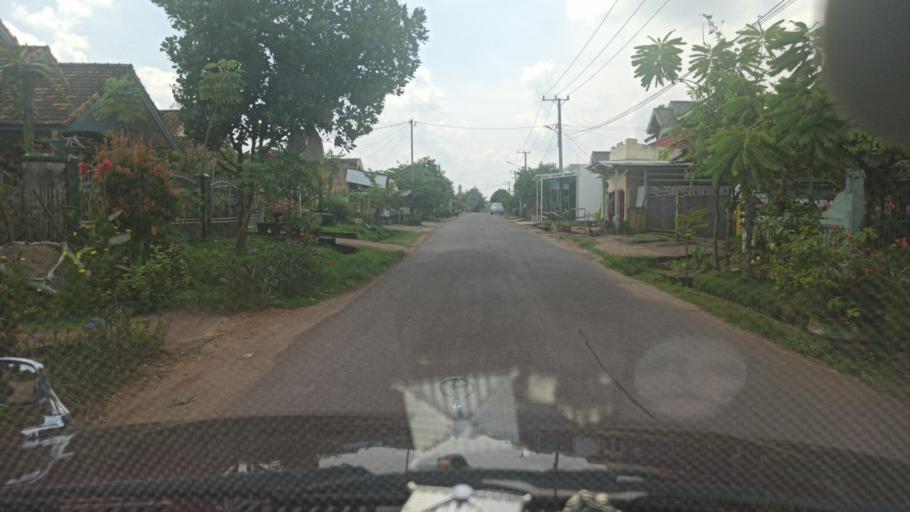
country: ID
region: South Sumatra
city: Gunungmenang
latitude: -3.3105
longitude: 104.1091
